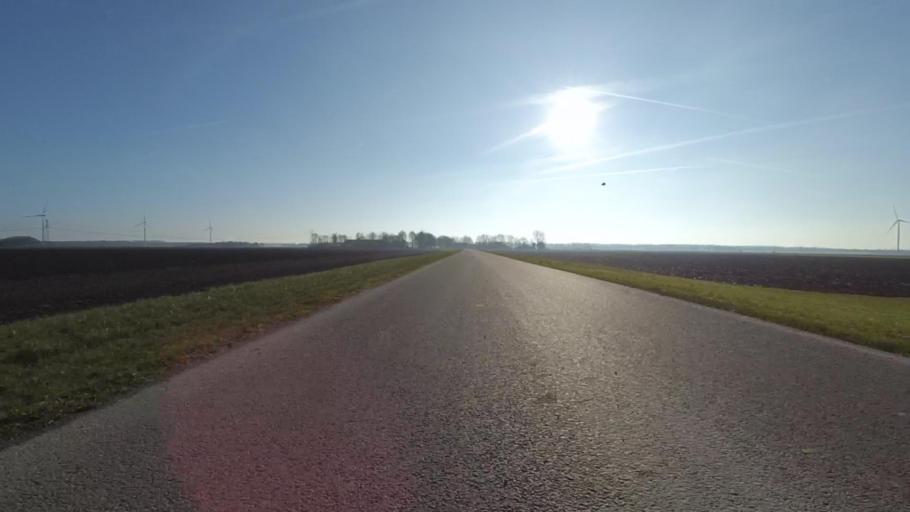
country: NL
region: Utrecht
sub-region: Gemeente Bunschoten
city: Bunschoten
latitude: 52.2937
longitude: 5.4286
